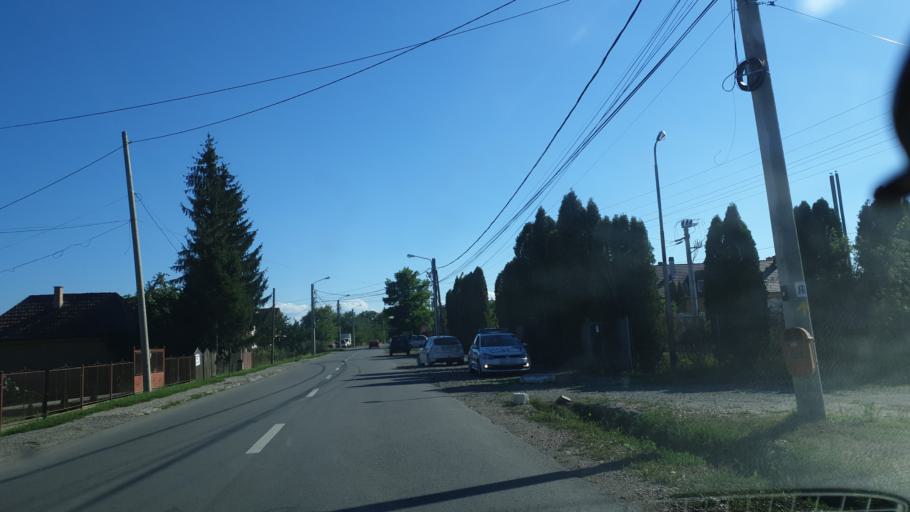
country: RO
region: Covasna
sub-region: Municipiul Sfantu Gheorghe
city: Sfantu-Gheorghe
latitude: 45.8491
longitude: 25.7776
